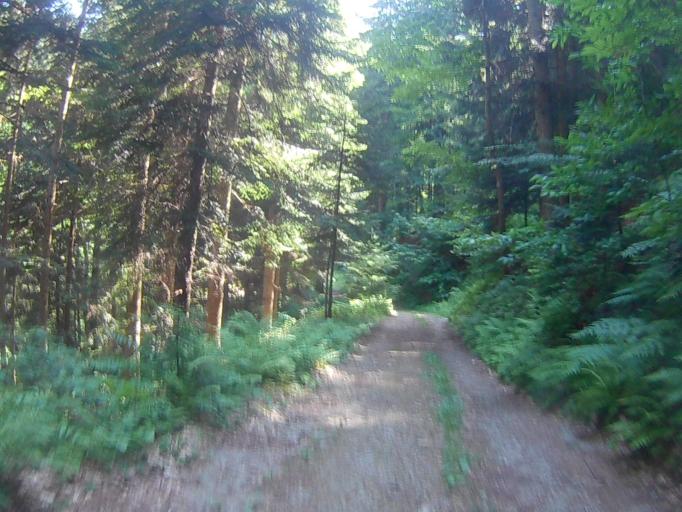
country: SI
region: Ruse
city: Ruse
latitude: 46.5123
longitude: 15.5152
